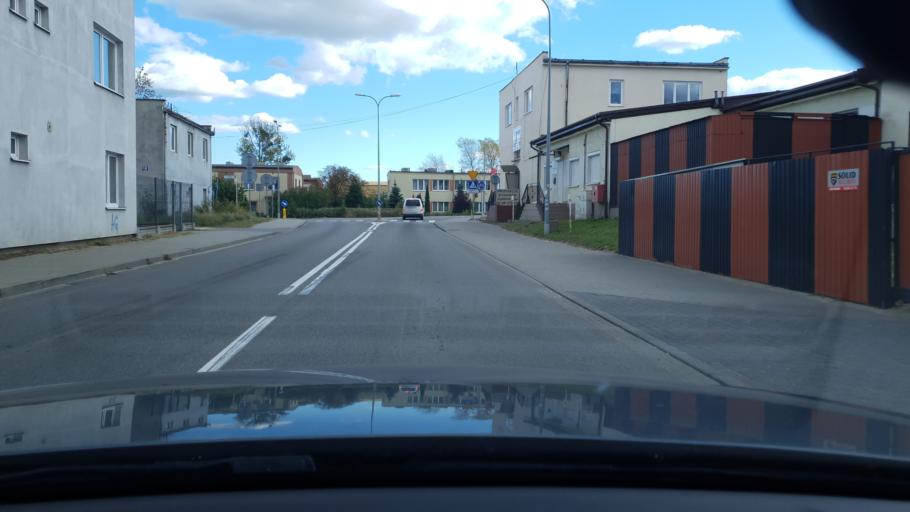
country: PL
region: Pomeranian Voivodeship
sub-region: Powiat wejherowski
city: Reda
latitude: 54.5995
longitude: 18.3461
